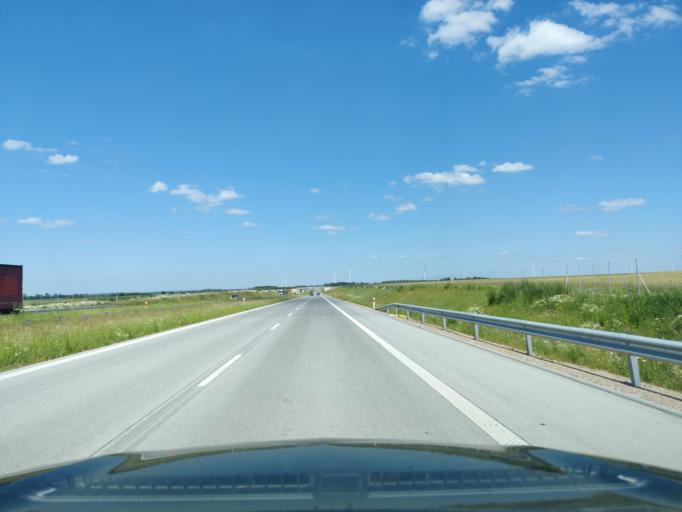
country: PL
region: Masovian Voivodeship
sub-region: Powiat mlawski
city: Wisniewo
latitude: 53.0197
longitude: 20.3409
